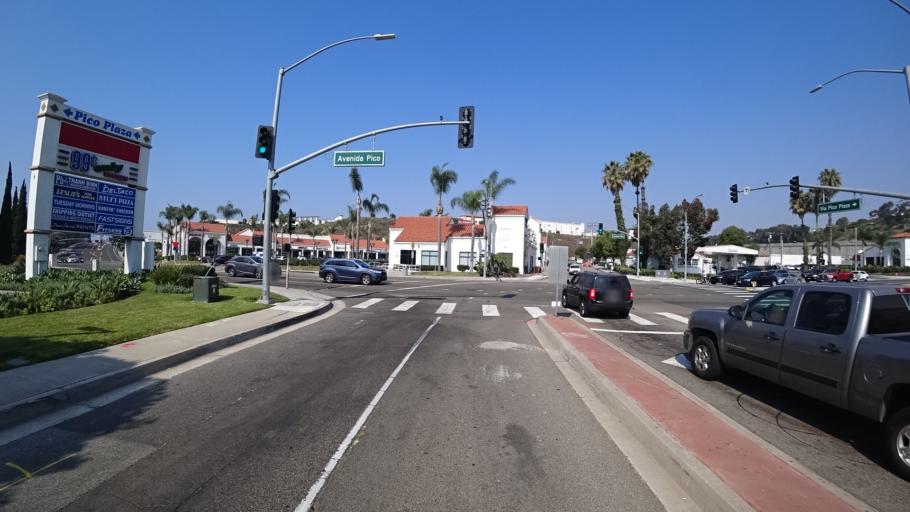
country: US
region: California
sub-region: Orange County
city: San Clemente
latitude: 33.4373
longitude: -117.6235
